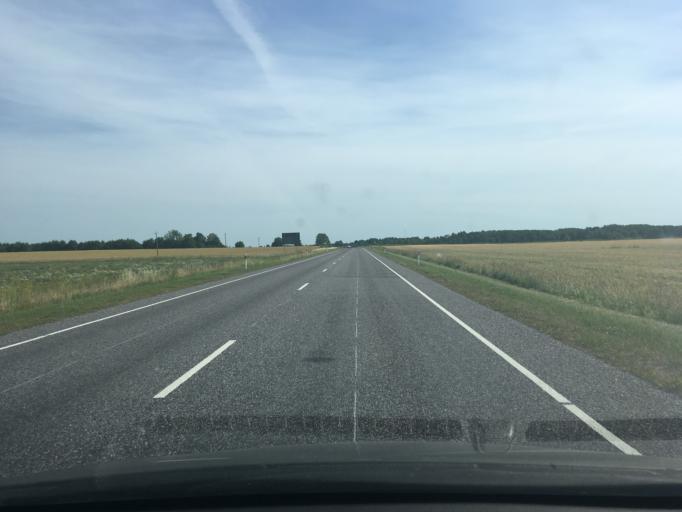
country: EE
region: Laeaene
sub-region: Lihula vald
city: Lihula
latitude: 58.6808
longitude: 23.7959
